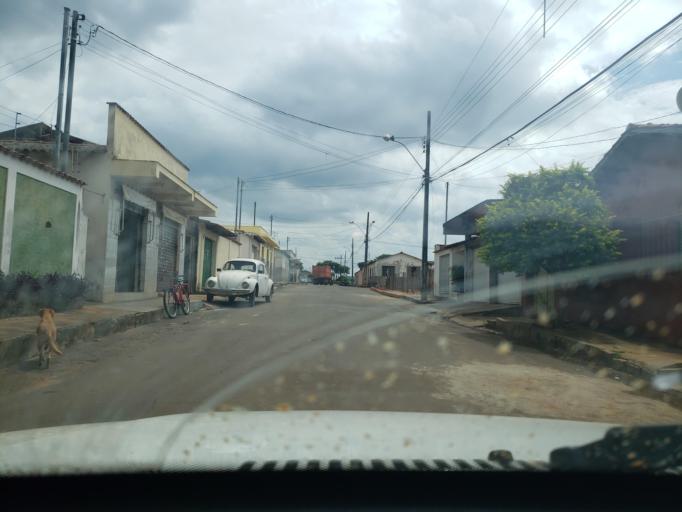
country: BR
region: Minas Gerais
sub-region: Boa Esperanca
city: Boa Esperanca
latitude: -21.0817
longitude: -45.5760
